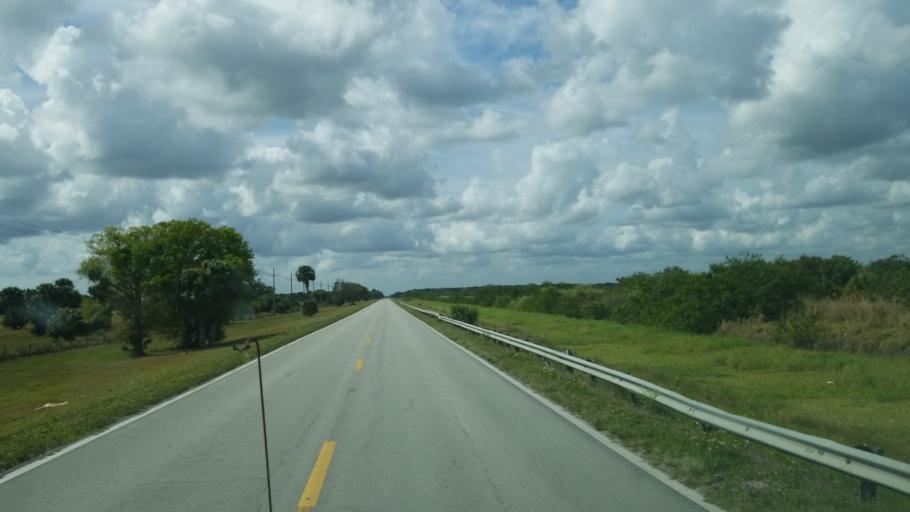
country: US
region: Florida
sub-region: Saint Lucie County
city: Lakewood Park
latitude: 27.4480
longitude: -80.5478
